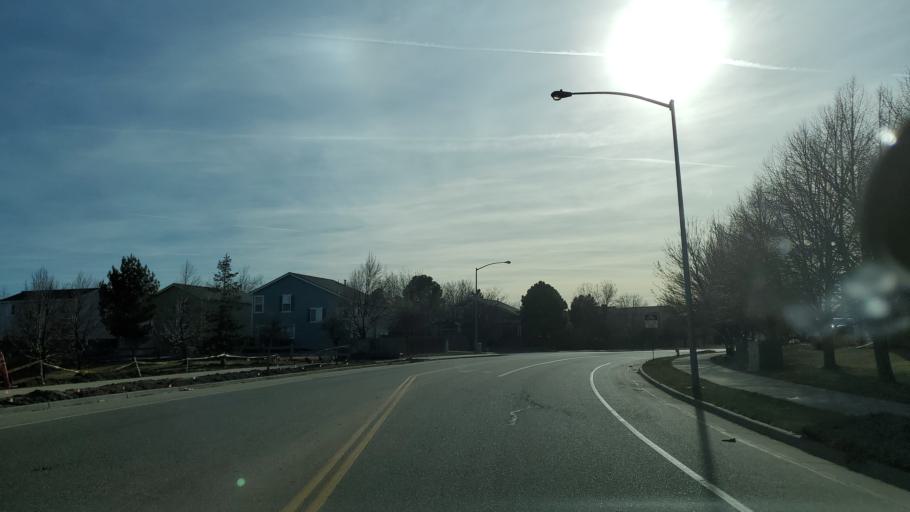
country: US
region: Colorado
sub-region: Adams County
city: Northglenn
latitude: 39.9123
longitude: -104.9534
